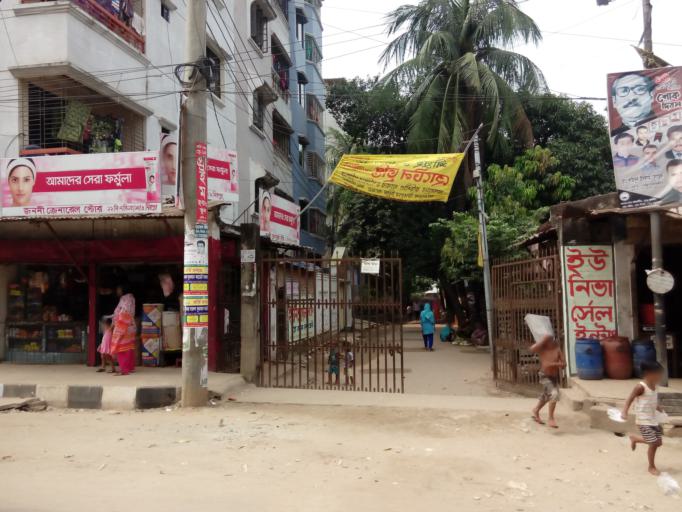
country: BD
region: Dhaka
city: Tungi
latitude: 23.8147
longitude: 90.3749
